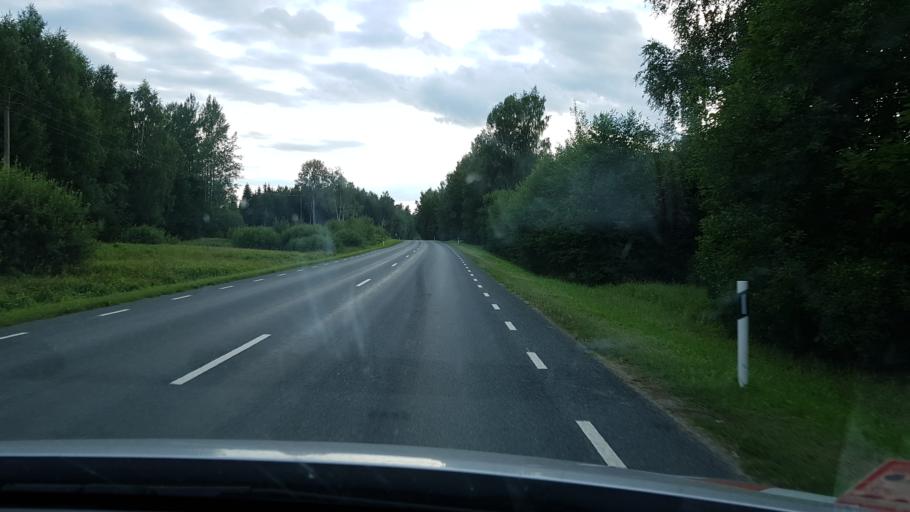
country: EE
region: Vorumaa
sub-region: Antsla vald
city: Vana-Antsla
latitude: 57.9503
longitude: 26.4237
